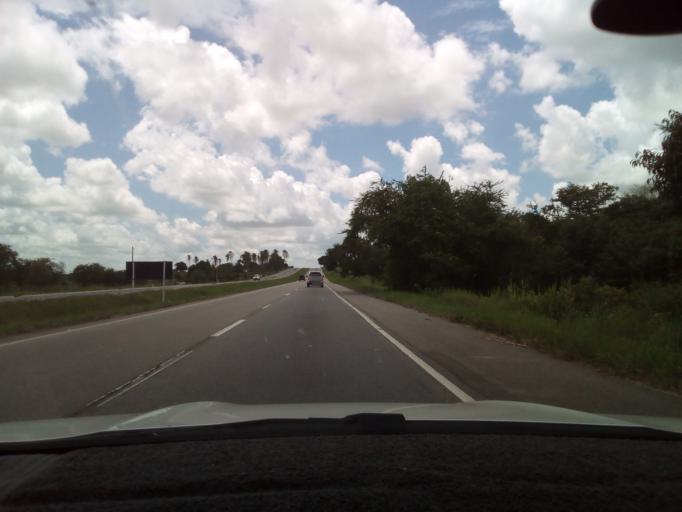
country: BR
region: Paraiba
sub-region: Pilar
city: Pilar
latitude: -7.1906
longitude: -35.2454
